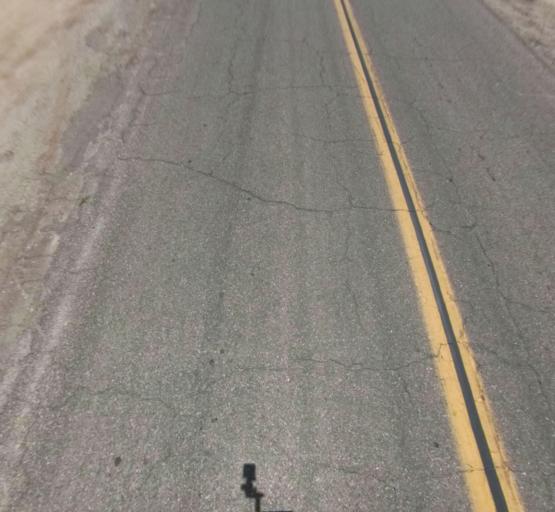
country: US
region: California
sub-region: Madera County
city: Parkwood
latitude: 36.8660
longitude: -120.0922
